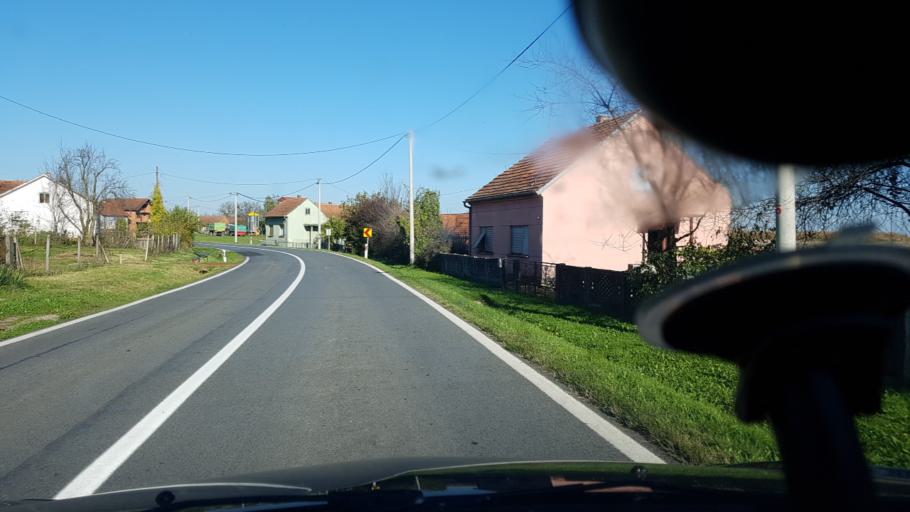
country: HR
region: Bjelovarsko-Bilogorska
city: Gudovac
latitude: 45.8333
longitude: 16.7722
